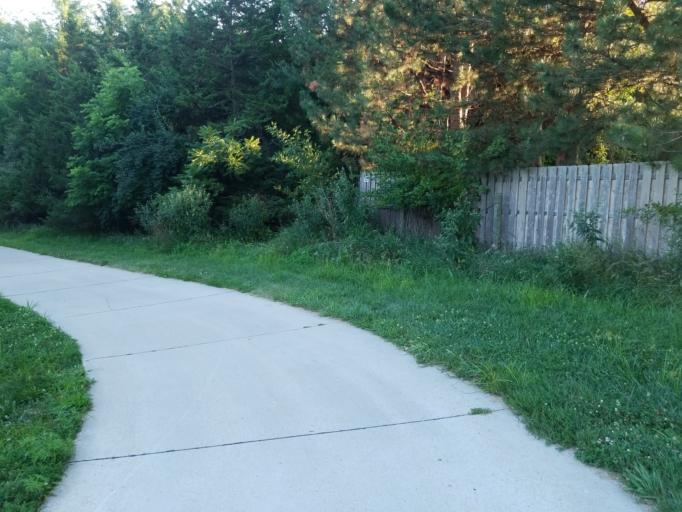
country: US
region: Nebraska
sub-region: Sarpy County
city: Chalco
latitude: 41.2246
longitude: -96.1745
